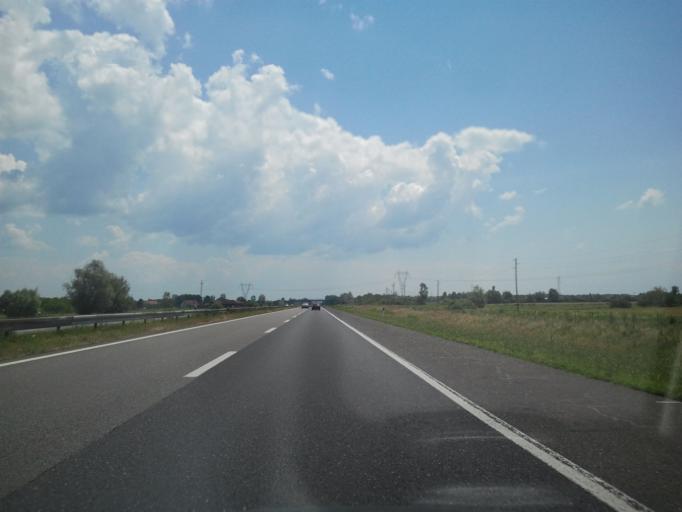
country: HR
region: Zagrebacka
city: Novoselec
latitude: 45.6301
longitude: 16.5213
